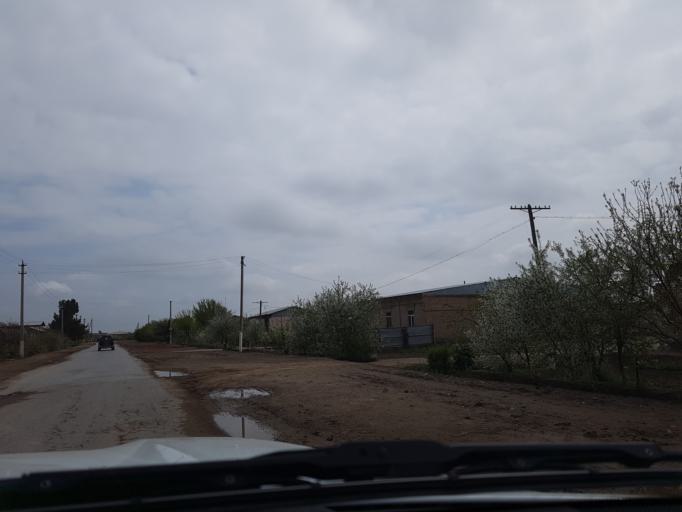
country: TM
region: Lebap
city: Turkmenabat
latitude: 38.9717
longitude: 63.6833
